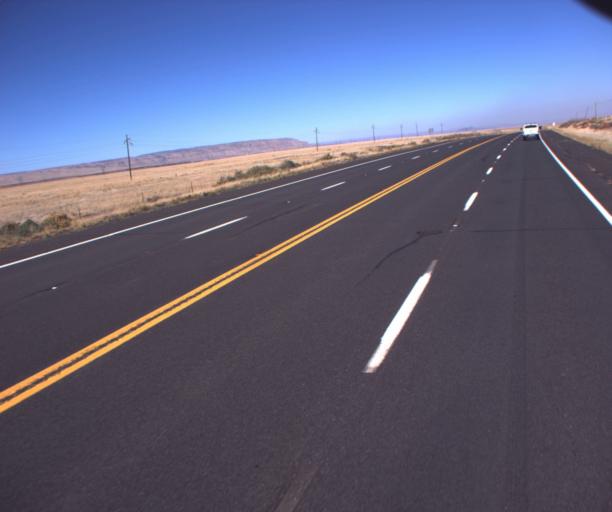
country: US
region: Arizona
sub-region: Coconino County
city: Flagstaff
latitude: 35.6488
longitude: -111.5164
